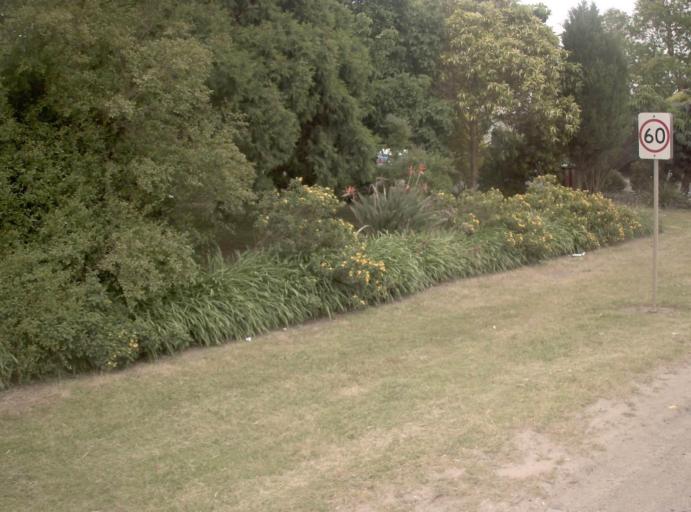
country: AU
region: Victoria
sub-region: Casey
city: Lynbrook
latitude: -38.0439
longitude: 145.2655
